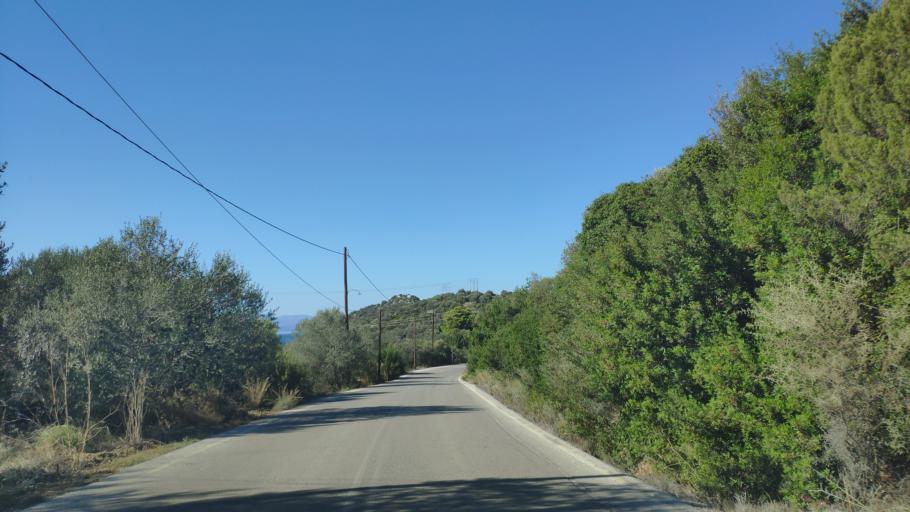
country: GR
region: Attica
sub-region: Nomos Piraios
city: Galatas
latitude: 37.5500
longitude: 23.3730
